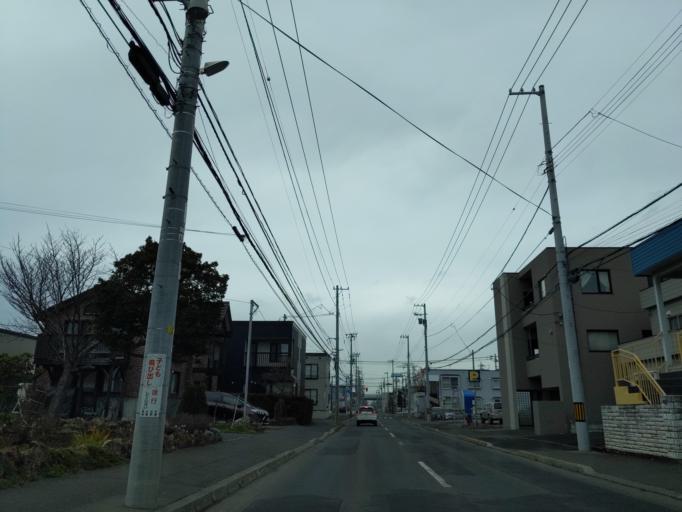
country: JP
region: Hokkaido
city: Sapporo
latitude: 43.0900
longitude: 141.3999
